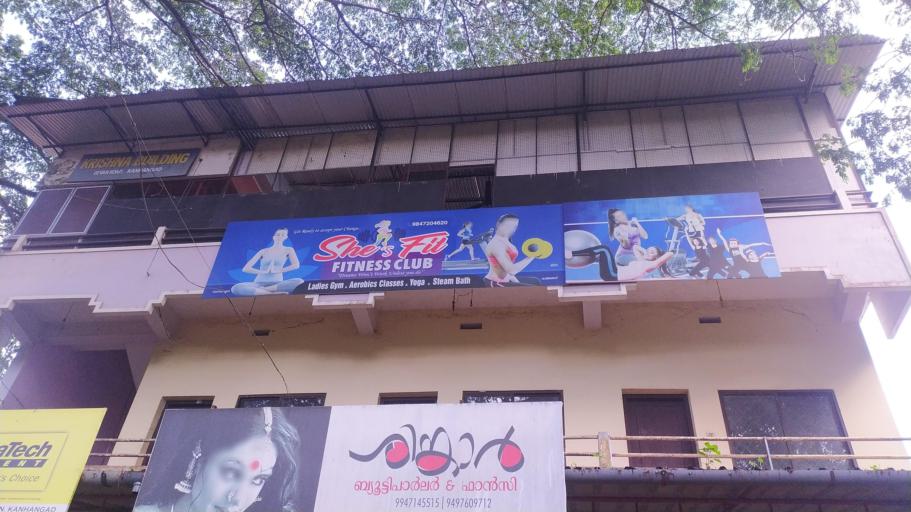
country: IN
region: Kerala
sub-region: Kasaragod District
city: Kannangad
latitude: 12.3210
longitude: 75.0897
